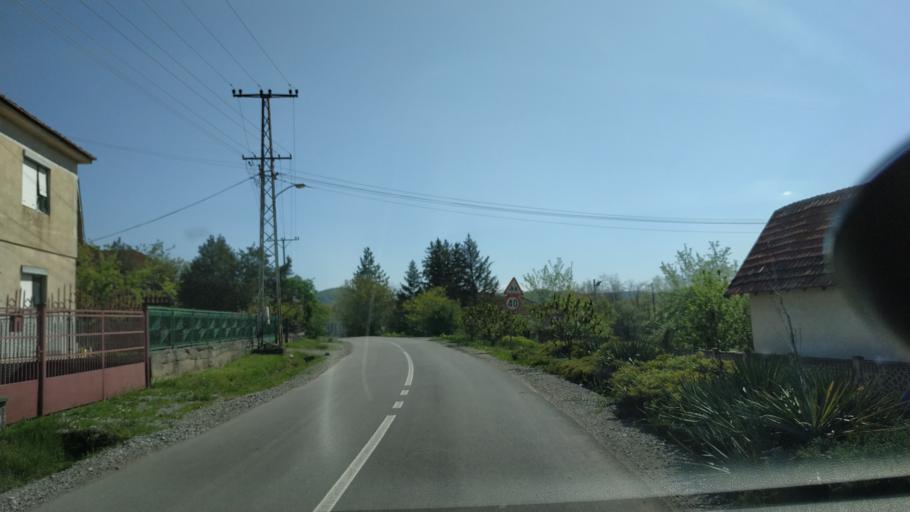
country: RS
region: Central Serbia
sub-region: Nisavski Okrug
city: Nis
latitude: 43.4481
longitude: 21.8476
